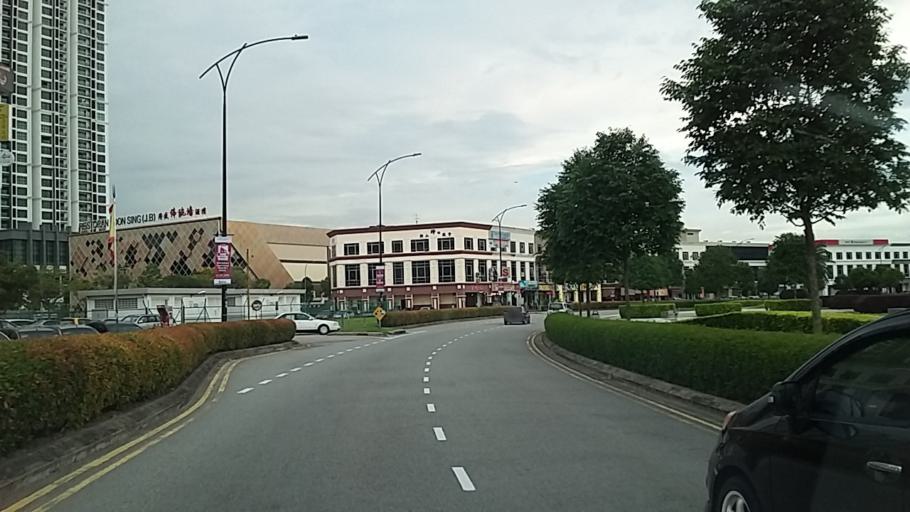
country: MY
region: Johor
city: Skudai
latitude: 1.4811
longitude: 103.6585
